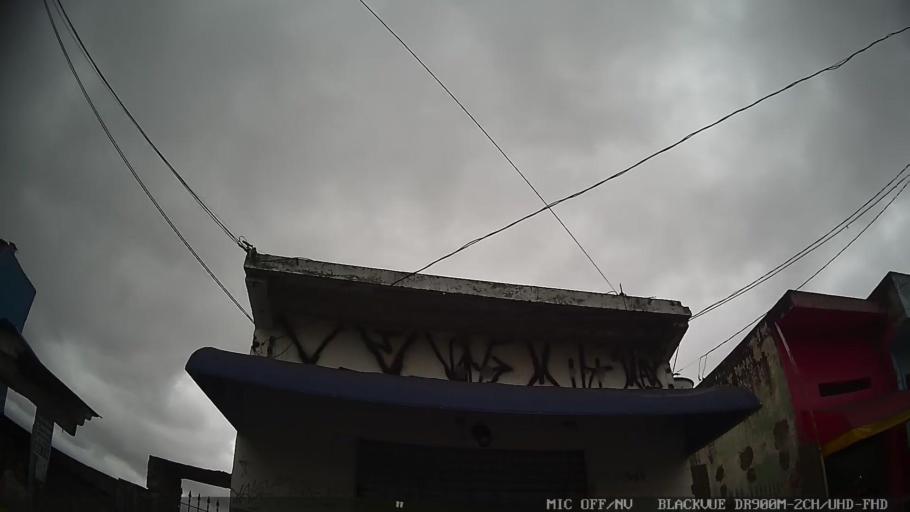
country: BR
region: Sao Paulo
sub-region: Osasco
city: Osasco
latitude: -23.4802
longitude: -46.7129
